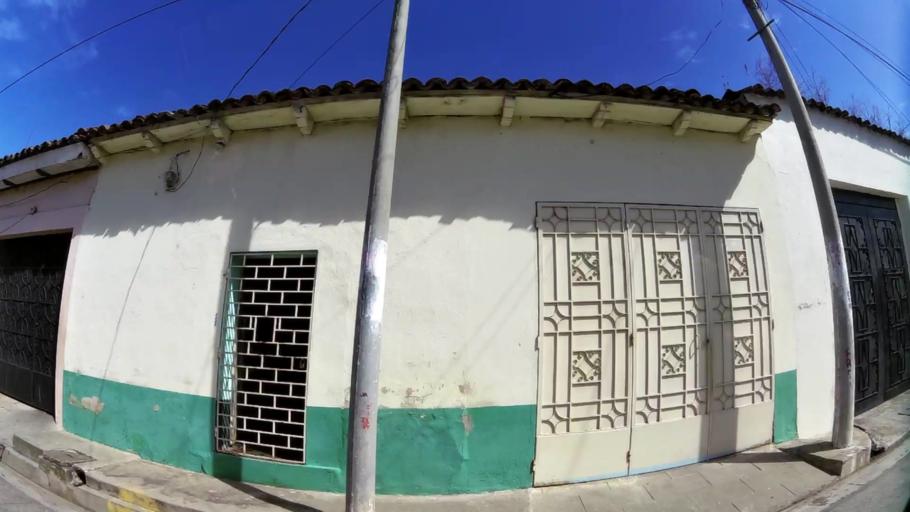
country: SV
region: Santa Ana
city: Chalchuapa
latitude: 13.9824
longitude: -89.6786
